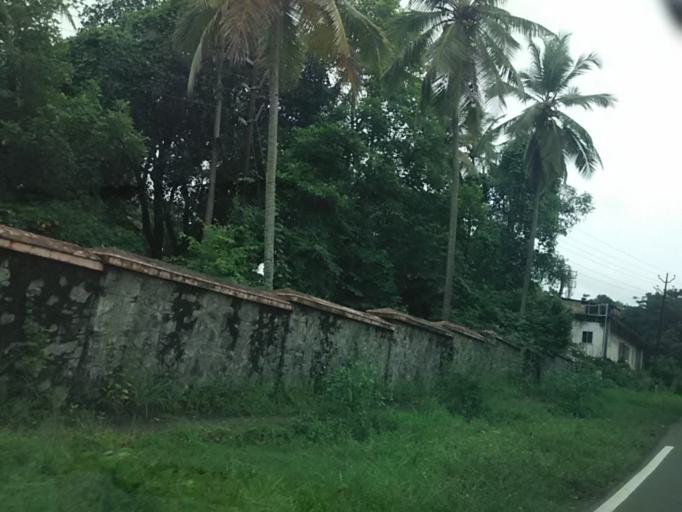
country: IN
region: Kerala
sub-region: Kozhikode
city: Mavoor
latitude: 11.3175
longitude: 75.9301
